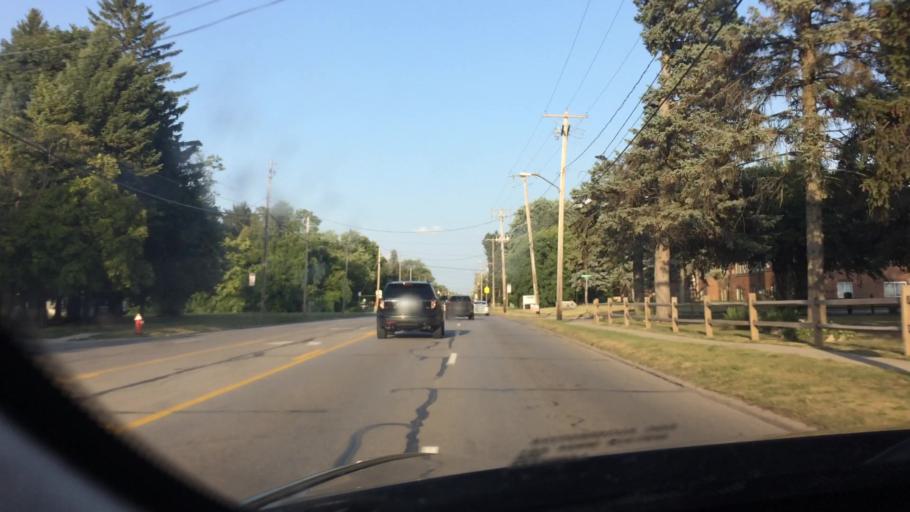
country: US
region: Ohio
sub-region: Lucas County
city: Ottawa Hills
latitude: 41.6536
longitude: -83.6797
